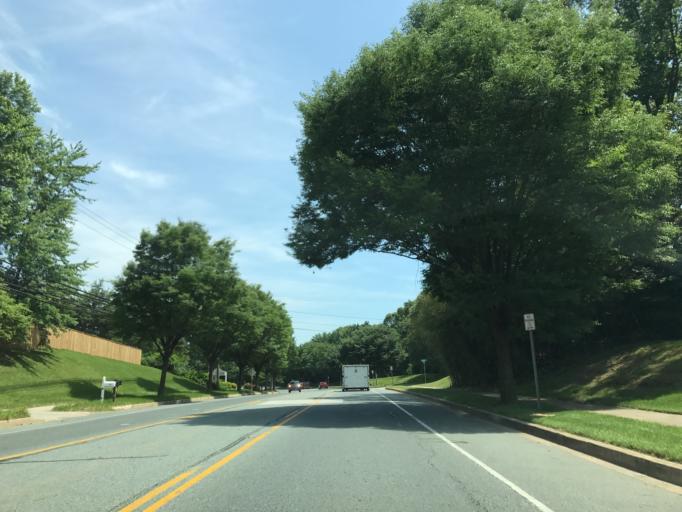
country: US
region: Maryland
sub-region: Anne Arundel County
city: Arden on the Severn
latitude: 39.0805
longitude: -76.5792
